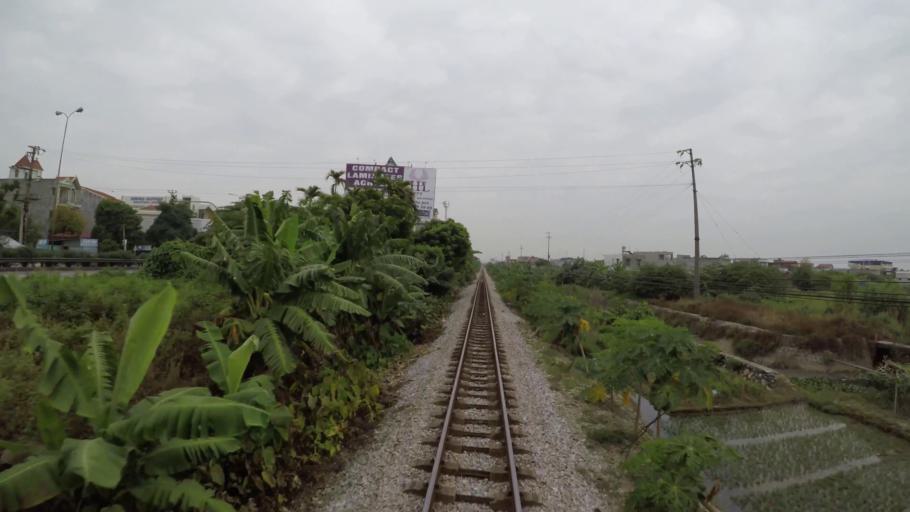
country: VN
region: Hai Duong
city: Phu Thai
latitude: 20.9171
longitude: 106.5629
